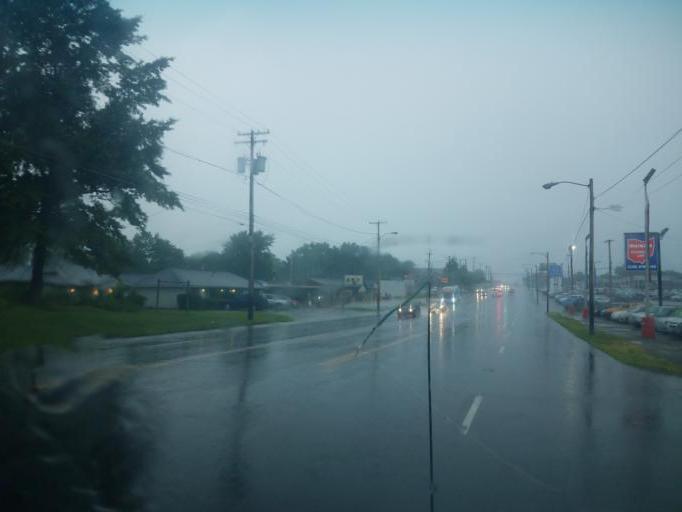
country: US
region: Ohio
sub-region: Stark County
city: Genoa
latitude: 40.7935
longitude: -81.4577
